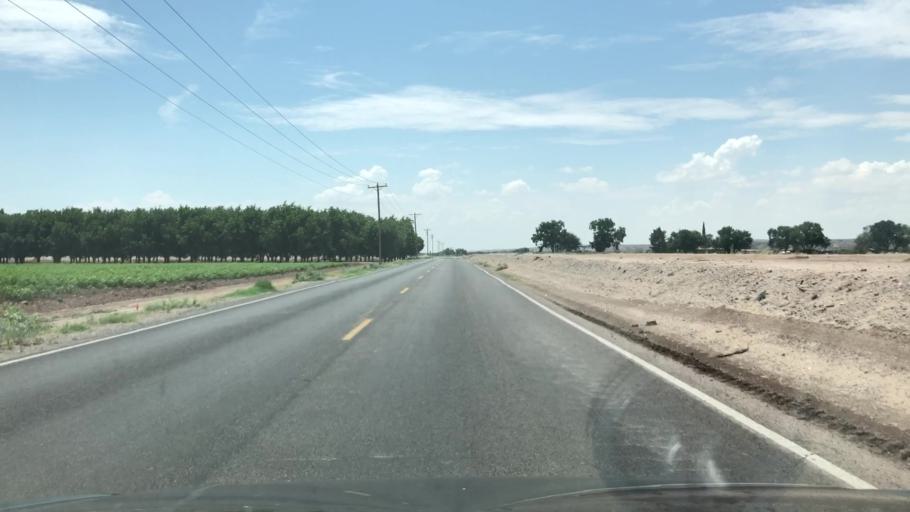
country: US
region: New Mexico
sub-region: Dona Ana County
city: Vado
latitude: 32.0787
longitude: -106.6836
